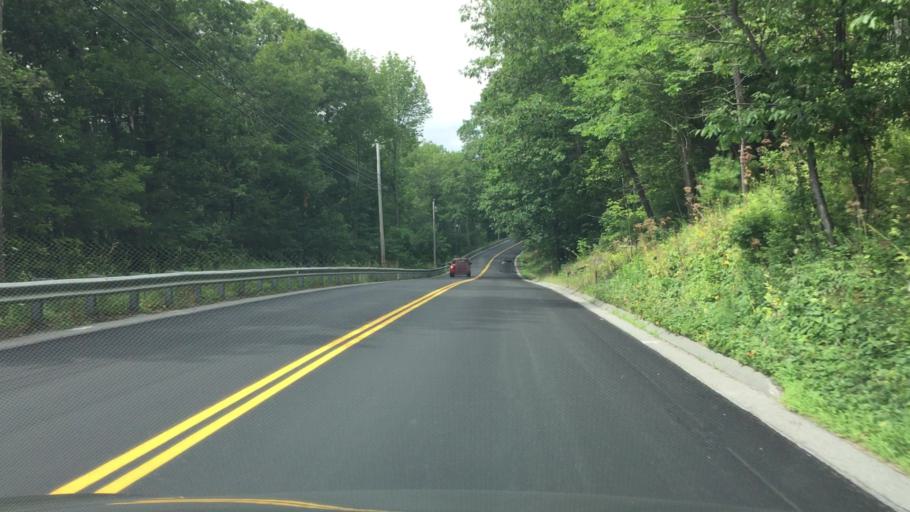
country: US
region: Maine
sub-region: Waldo County
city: Winterport
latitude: 44.6112
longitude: -68.8230
